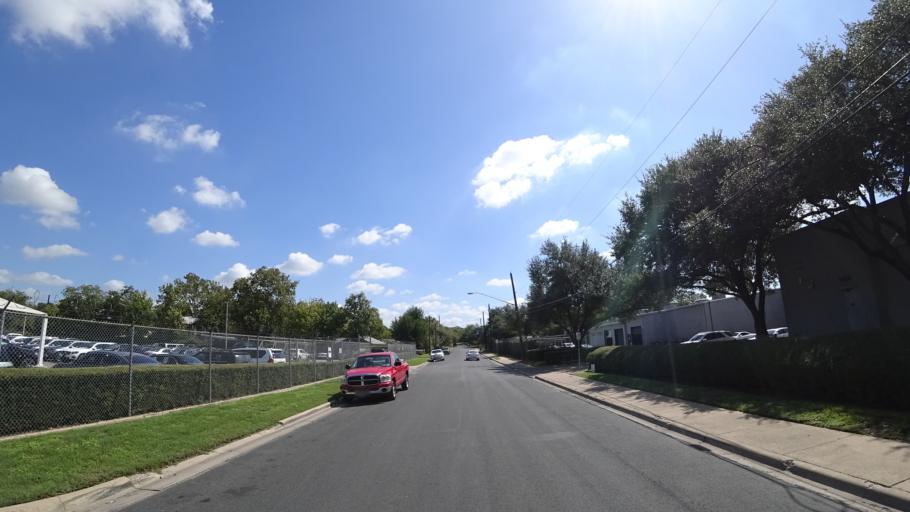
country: US
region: Texas
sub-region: Travis County
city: Austin
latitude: 30.3333
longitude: -97.7156
